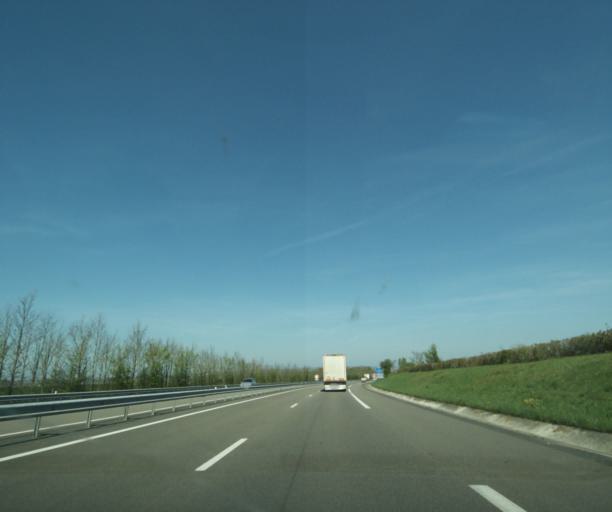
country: FR
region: Bourgogne
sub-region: Departement de la Nievre
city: Challuy
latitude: 46.9340
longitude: 3.1570
